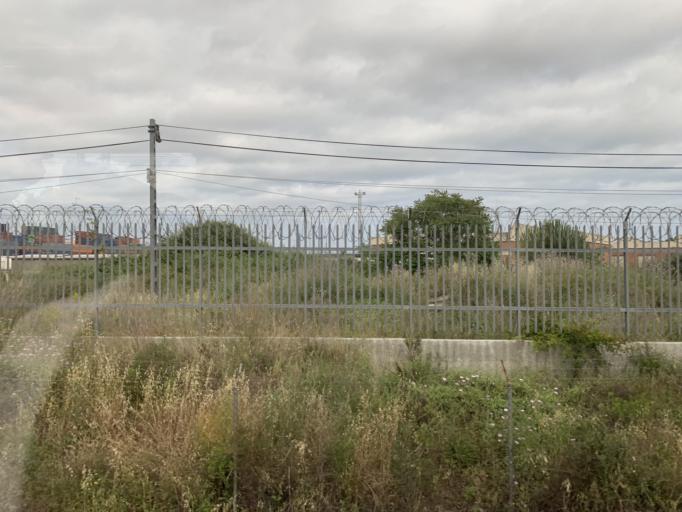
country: ES
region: Catalonia
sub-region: Provincia de Barcelona
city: L'Hospitalet de Llobregat
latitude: 41.3433
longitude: 2.1144
